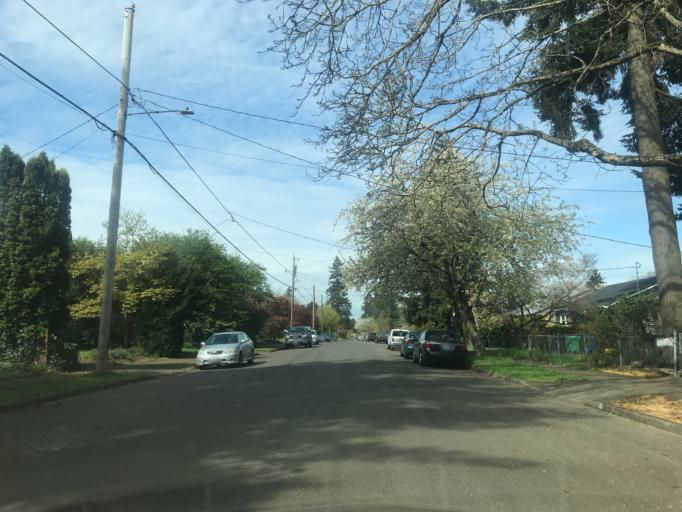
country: US
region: Oregon
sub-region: Multnomah County
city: Lents
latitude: 45.4801
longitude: -122.5999
